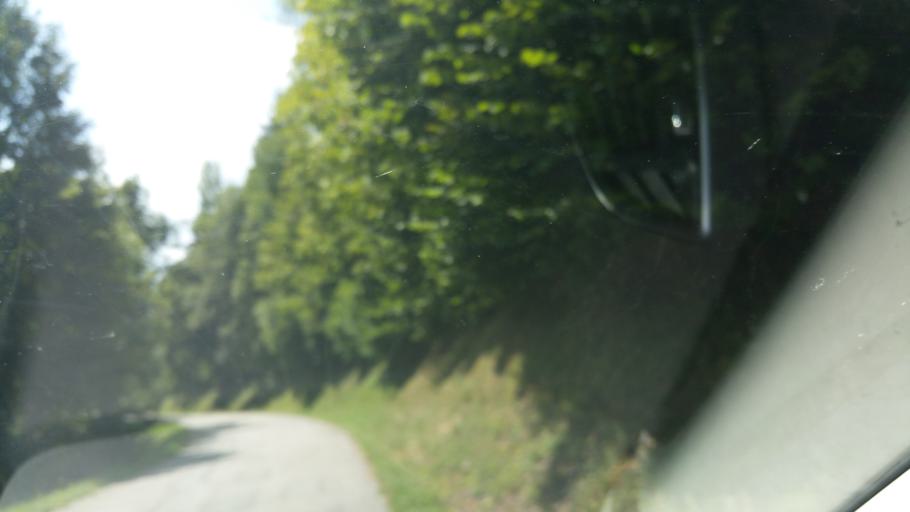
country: FR
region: Rhone-Alpes
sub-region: Departement de la Savoie
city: La Chambre
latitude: 45.4091
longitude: 6.3347
